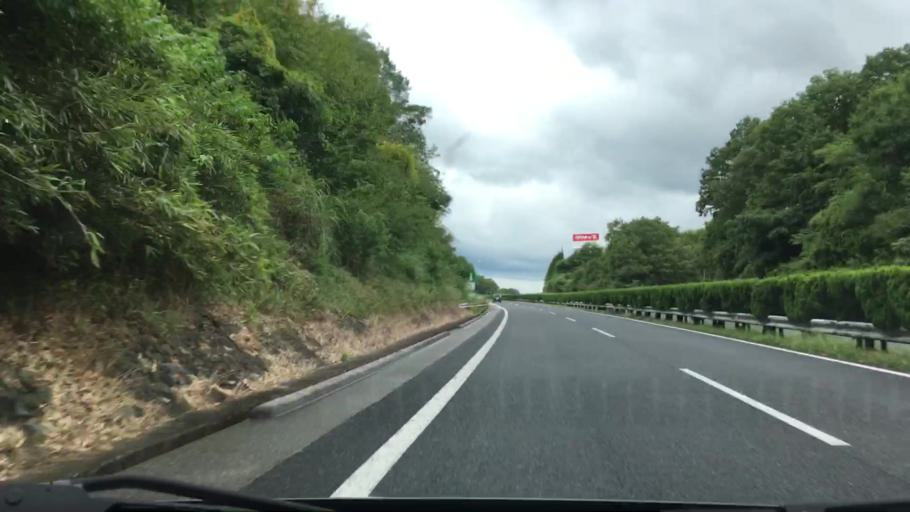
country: JP
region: Okayama
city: Tsuyama
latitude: 35.0446
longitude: 134.1109
